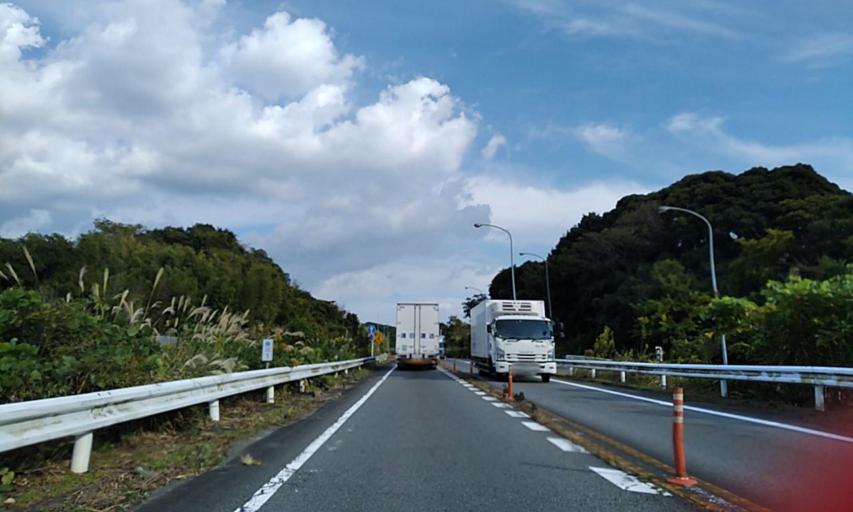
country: JP
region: Shizuoka
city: Kakegawa
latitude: 34.7863
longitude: 138.0523
